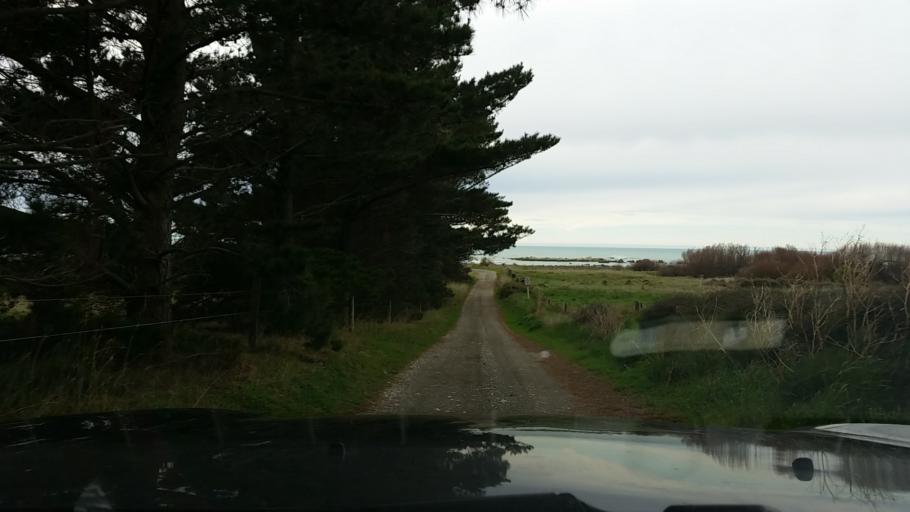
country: NZ
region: Marlborough
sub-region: Marlborough District
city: Blenheim
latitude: -41.9256
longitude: 174.0940
